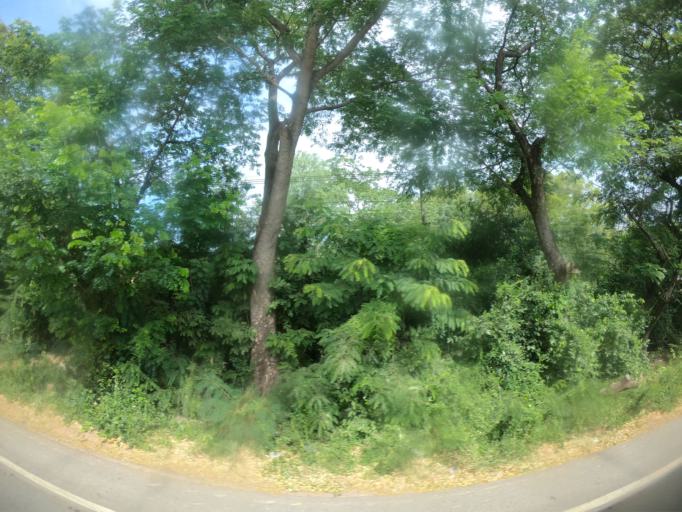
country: TH
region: Maha Sarakham
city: Chiang Yuen
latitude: 16.3438
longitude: 103.1428
